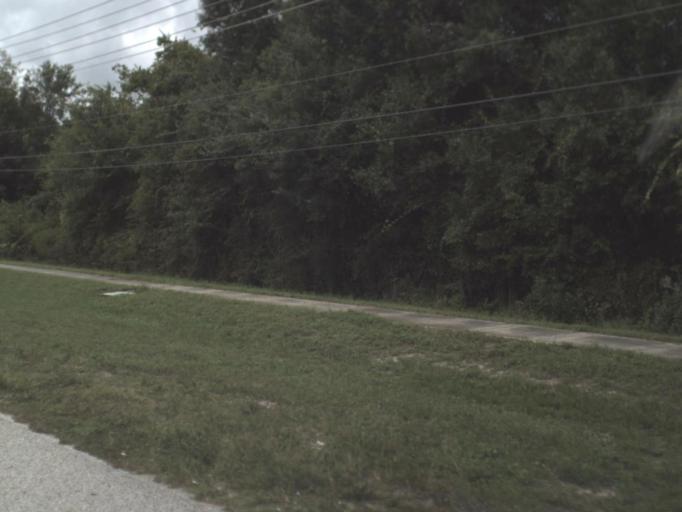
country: US
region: Florida
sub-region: Pasco County
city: Trinity
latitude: 28.1637
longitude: -82.6978
